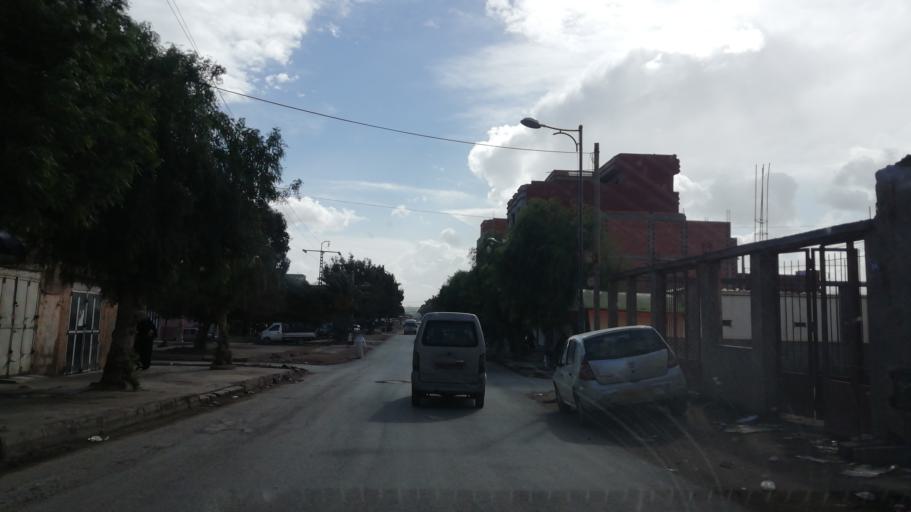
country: DZ
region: Oran
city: Sidi ech Chahmi
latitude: 35.6519
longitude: -0.5671
